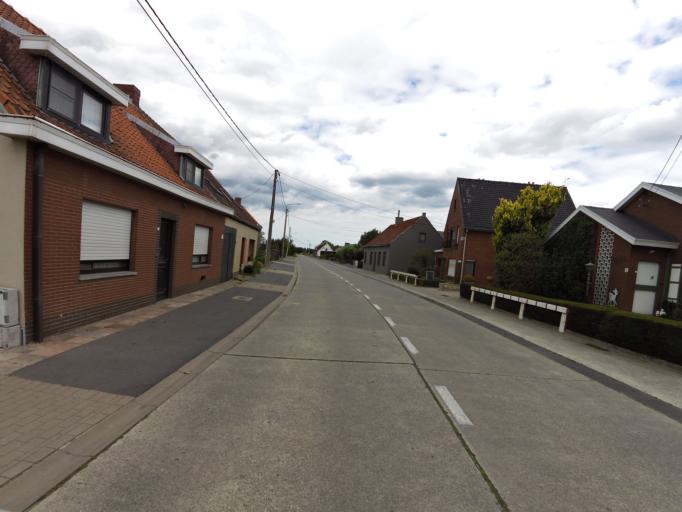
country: BE
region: Flanders
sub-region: Provincie West-Vlaanderen
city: Kortemark
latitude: 51.0033
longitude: 3.0525
